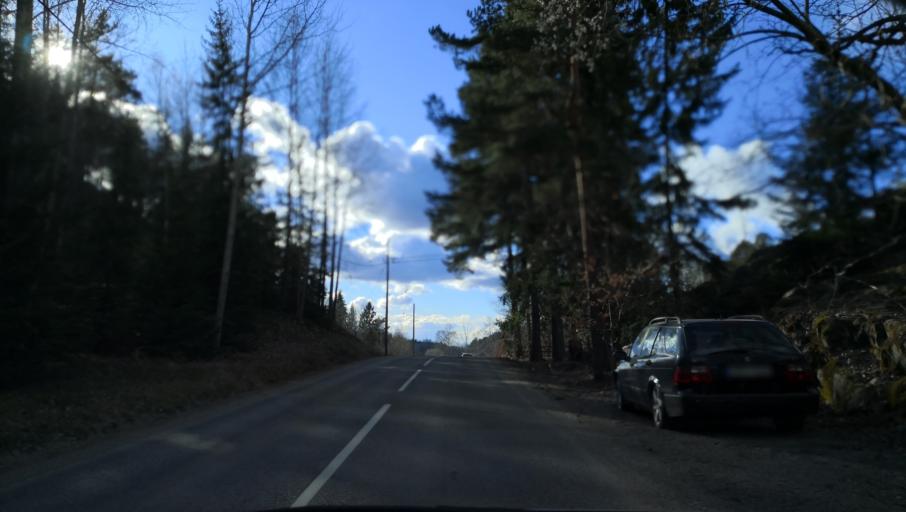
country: SE
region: Stockholm
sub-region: Varmdo Kommun
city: Mortnas
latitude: 59.2877
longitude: 18.4686
